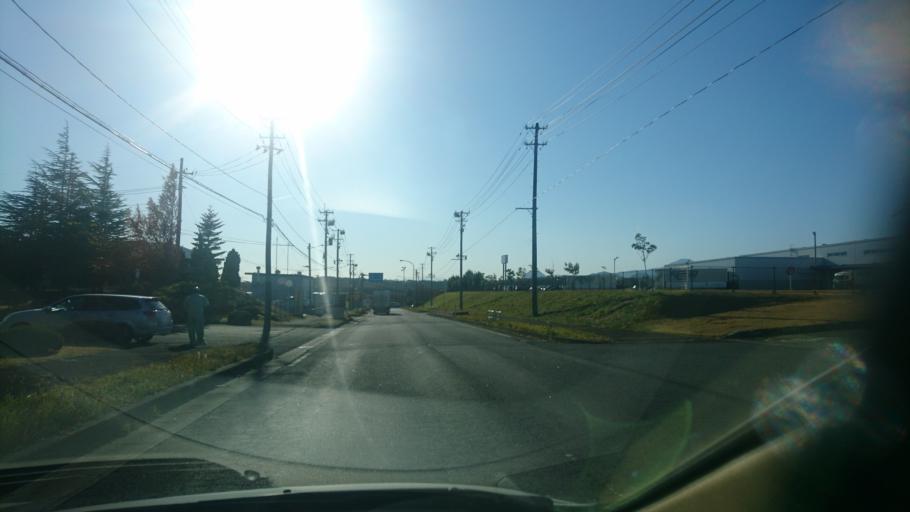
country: JP
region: Miyagi
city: Tomiya
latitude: 38.4559
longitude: 140.9348
